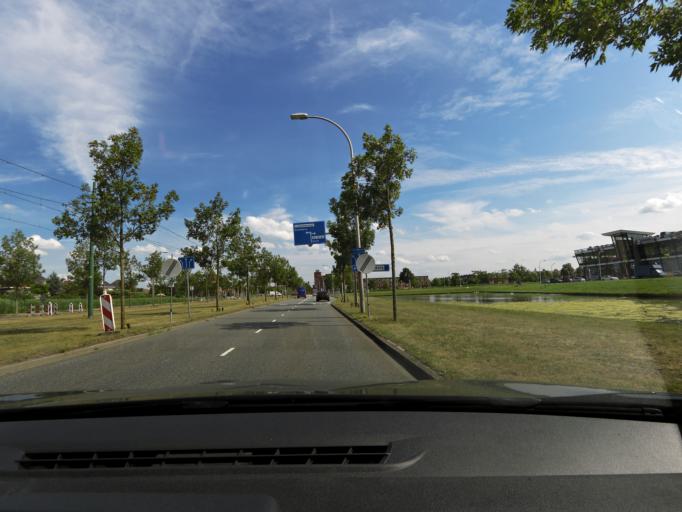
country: NL
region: South Holland
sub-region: Gemeente Den Haag
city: Ypenburg
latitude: 52.0438
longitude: 4.3619
